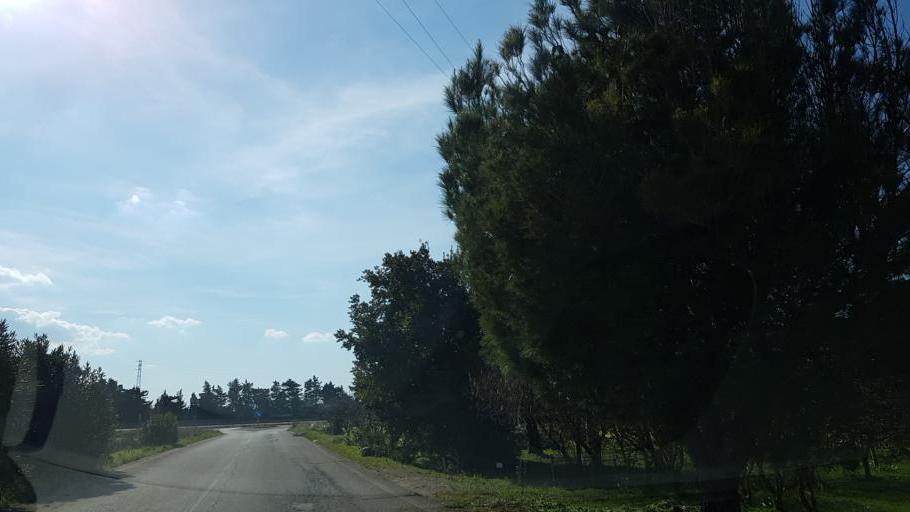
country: IT
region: Apulia
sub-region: Provincia di Brindisi
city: San Vito dei Normanni
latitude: 40.6912
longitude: 17.8241
